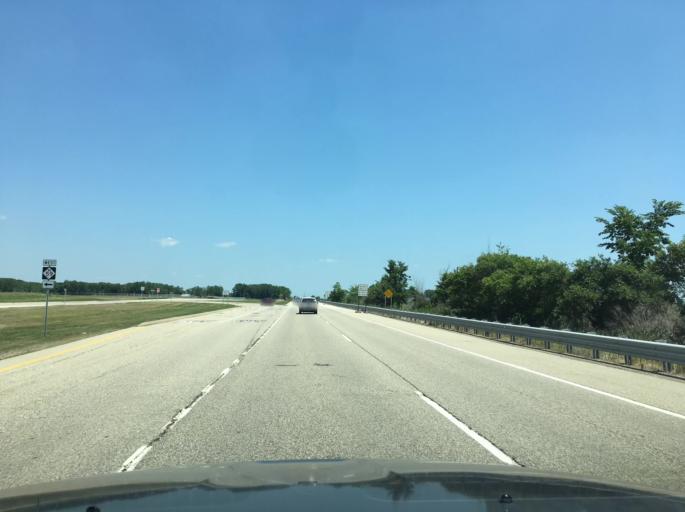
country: US
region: Michigan
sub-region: Macomb County
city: Mount Clemens
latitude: 42.6302
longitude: -82.8429
